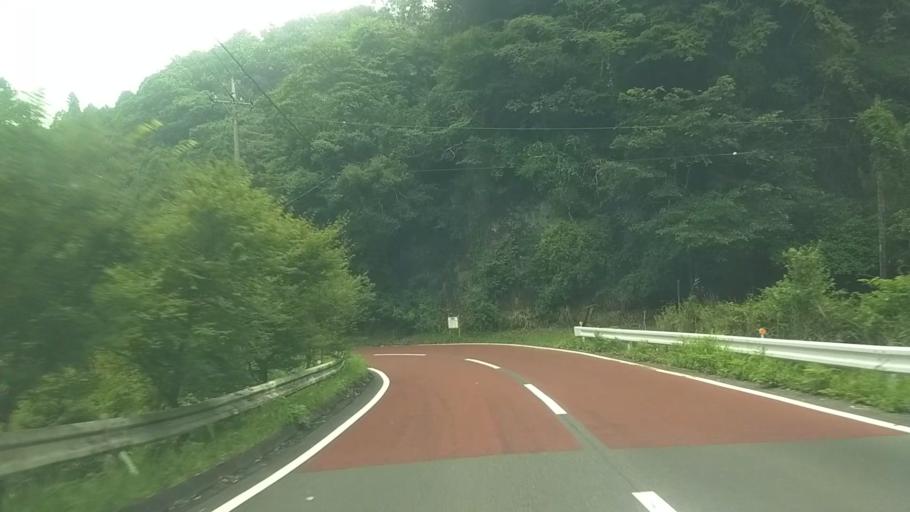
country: JP
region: Chiba
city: Kawaguchi
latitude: 35.2337
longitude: 140.0303
